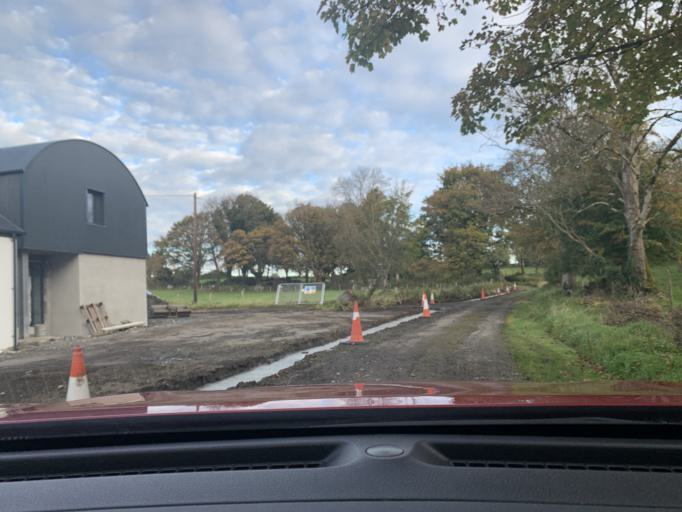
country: IE
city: Ballisodare
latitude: 54.2316
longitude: -8.5029
